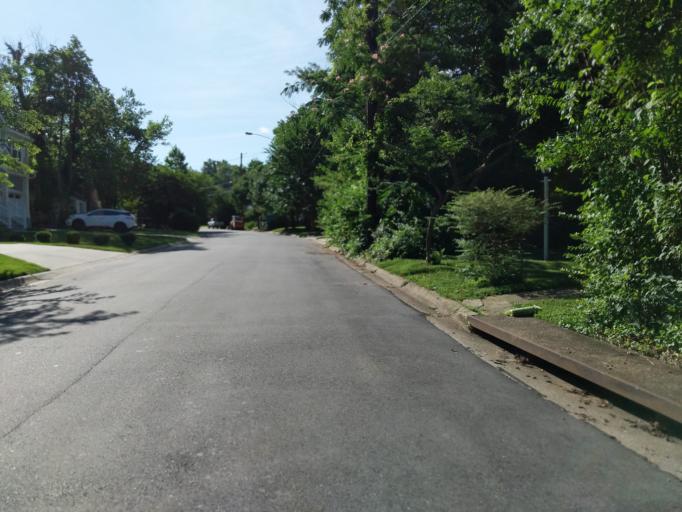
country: US
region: Maryland
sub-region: Montgomery County
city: Bethesda
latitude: 39.0023
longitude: -77.1183
